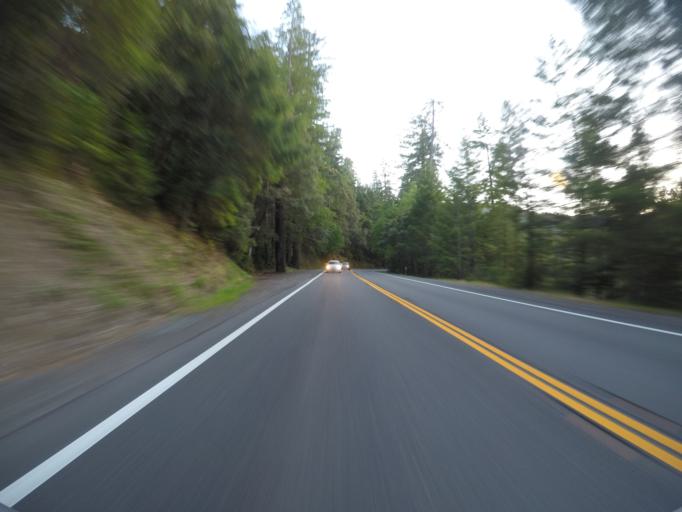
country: US
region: California
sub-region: Humboldt County
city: Redway
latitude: 39.9033
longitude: -123.7503
